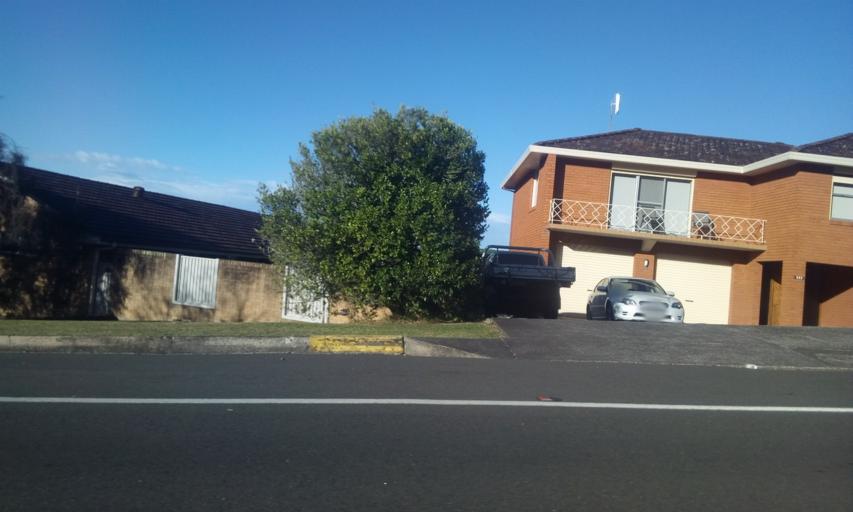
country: AU
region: New South Wales
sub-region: Wollongong
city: Mount Keira
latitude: -34.4286
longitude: 150.8477
